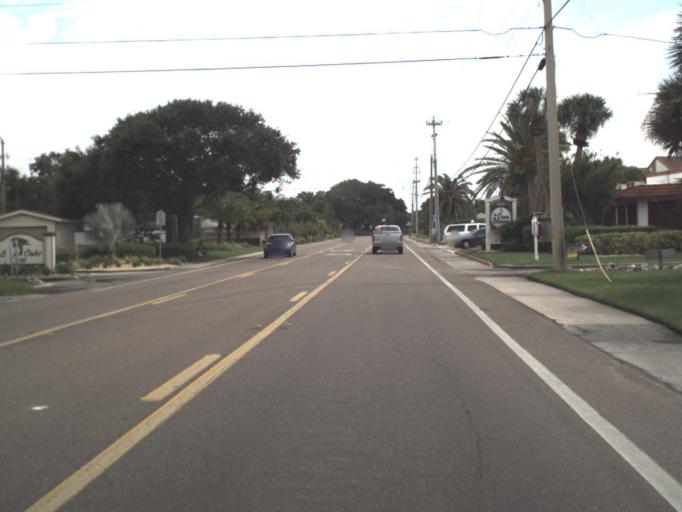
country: US
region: Florida
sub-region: Sarasota County
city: Gulf Gate Estates
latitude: 27.2590
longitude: -82.5387
